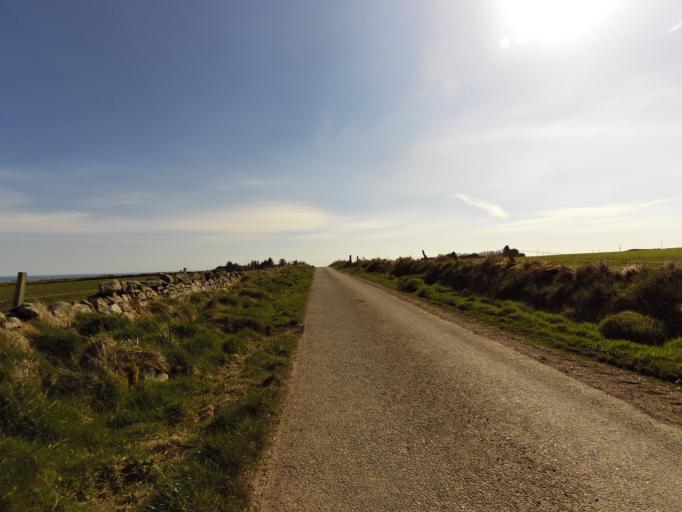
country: GB
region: Scotland
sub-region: Aberdeenshire
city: Portlethen
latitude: 57.0730
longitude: -2.1034
